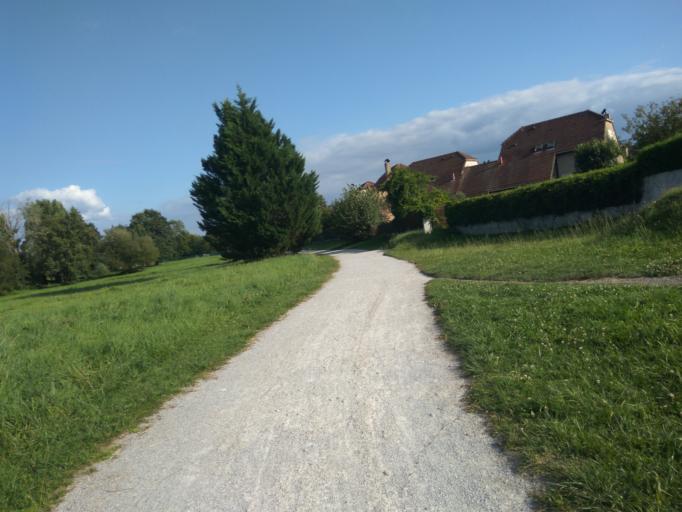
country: FR
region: Aquitaine
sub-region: Departement des Pyrenees-Atlantiques
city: Gelos
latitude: 43.2895
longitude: -0.3748
